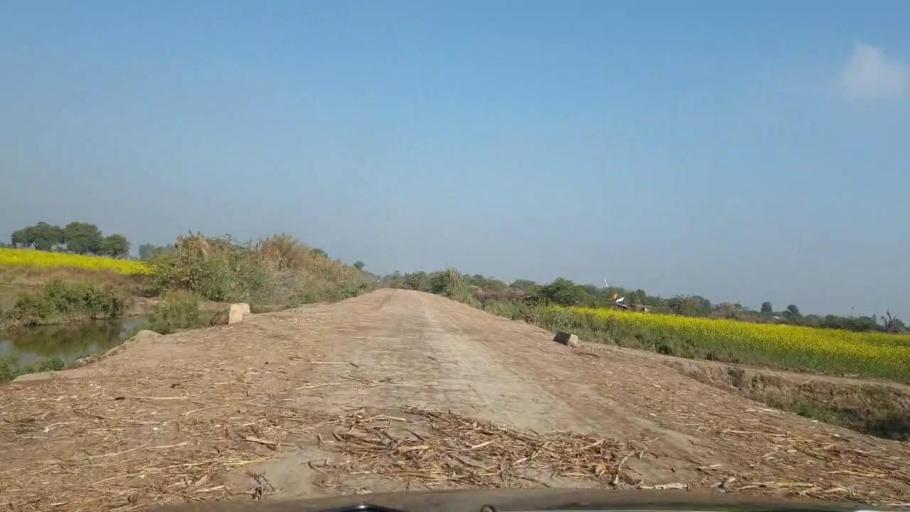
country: PK
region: Sindh
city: Sinjhoro
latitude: 26.0676
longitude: 68.7879
